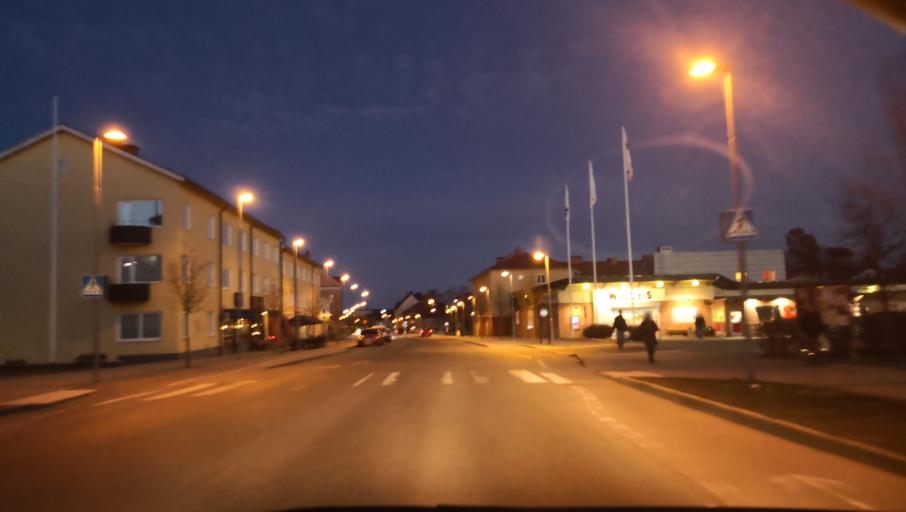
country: SE
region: Stockholm
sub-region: Nynashamns Kommun
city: Nynashamn
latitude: 58.9135
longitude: 17.9474
